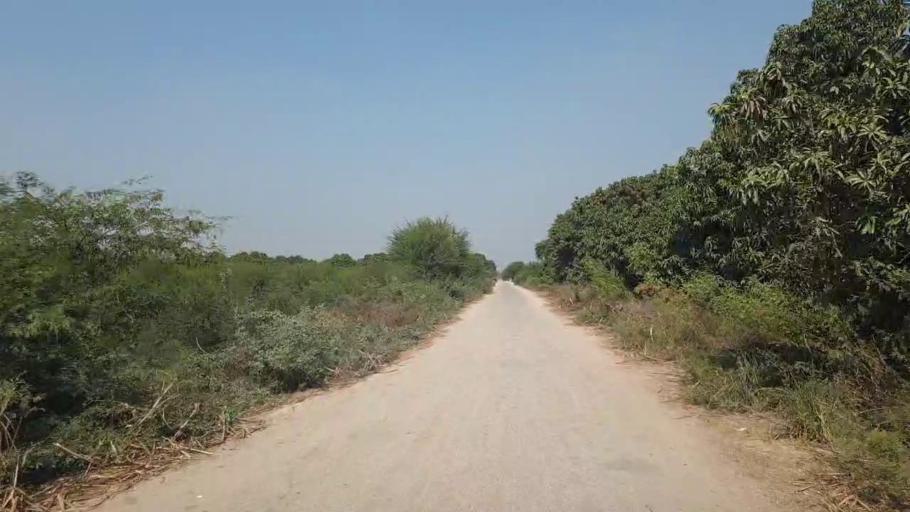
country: PK
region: Sindh
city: Chambar
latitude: 25.4043
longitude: 68.8878
